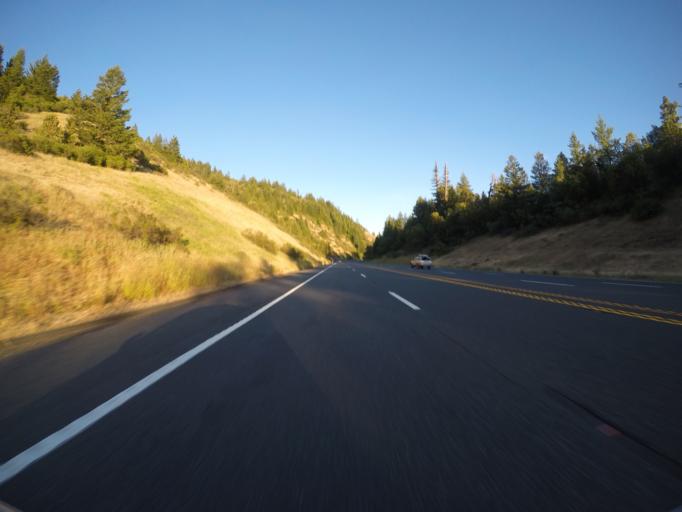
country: US
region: California
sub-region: Mendocino County
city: Laytonville
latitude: 39.8327
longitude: -123.6776
